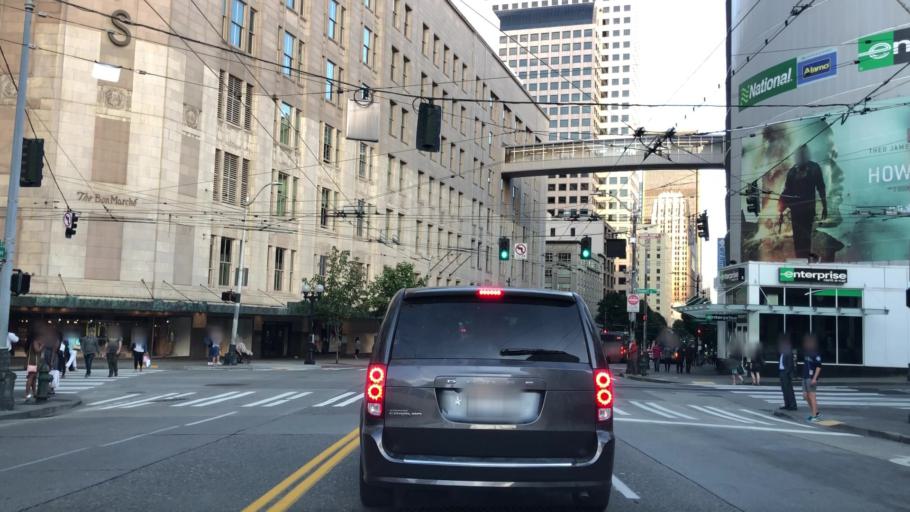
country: US
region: Washington
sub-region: King County
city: Seattle
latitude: 47.6118
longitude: -122.3400
